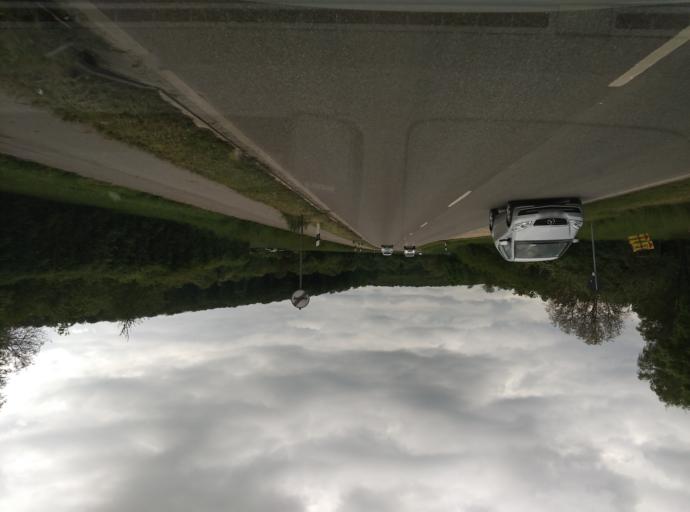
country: DE
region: Baden-Wuerttemberg
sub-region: Regierungsbezirk Stuttgart
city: Frickenhausen
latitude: 48.6059
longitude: 9.3496
